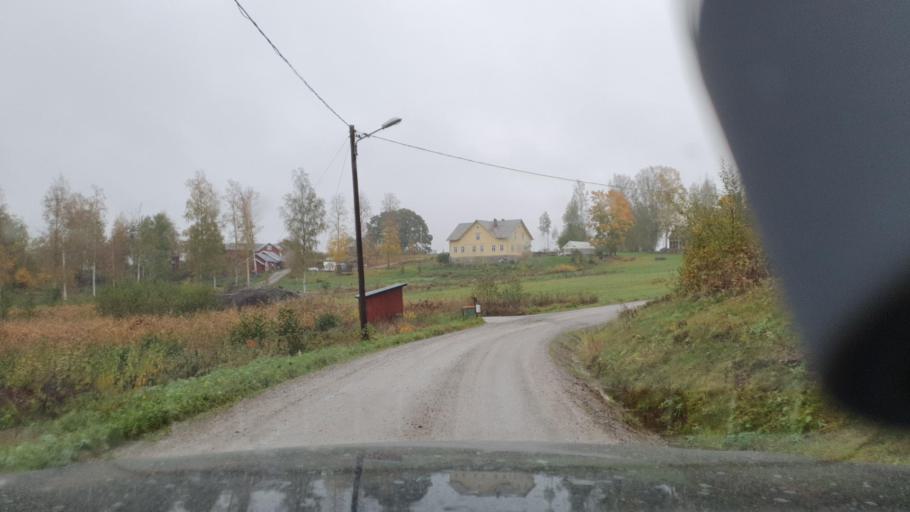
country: SE
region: Vaermland
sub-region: Karlstads Kommun
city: Edsvalla
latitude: 59.6046
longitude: 12.9188
